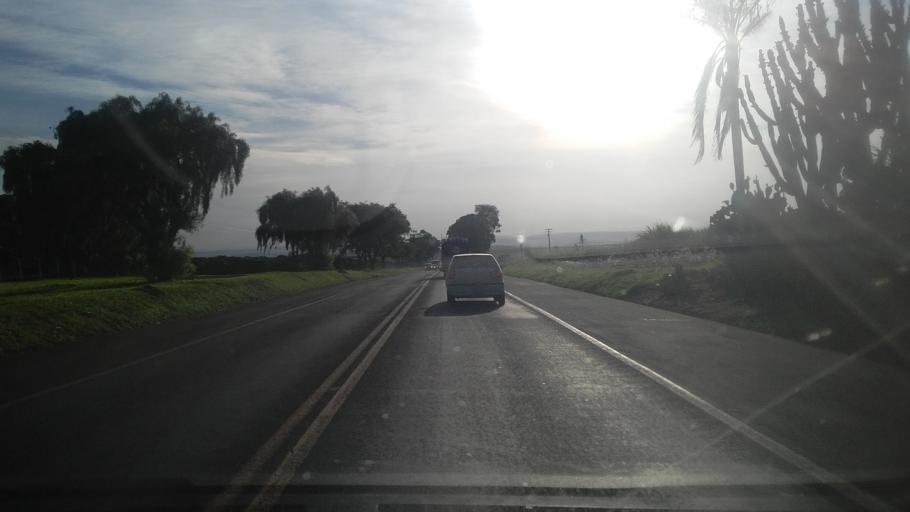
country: BR
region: Parana
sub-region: Bandeirantes
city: Bandeirantes
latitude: -23.1454
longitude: -50.5749
